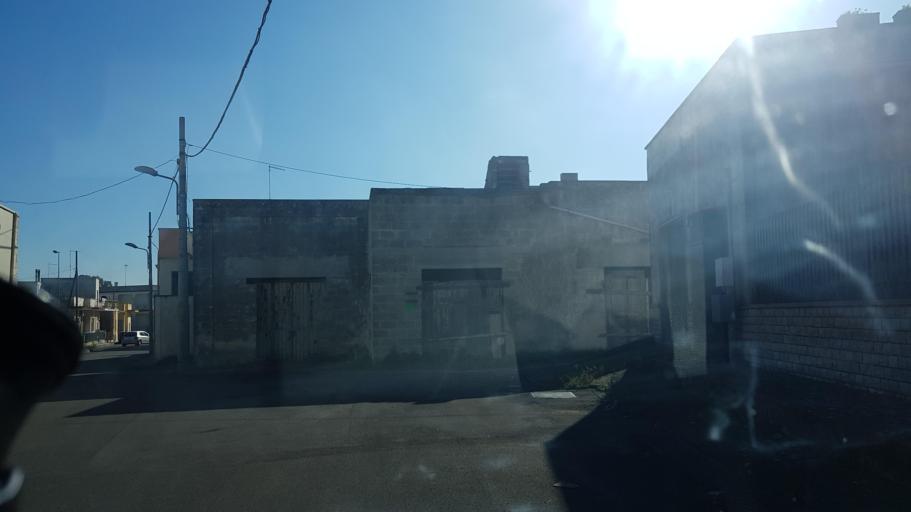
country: IT
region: Apulia
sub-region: Provincia di Lecce
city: Squinzano
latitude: 40.4316
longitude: 18.0457
